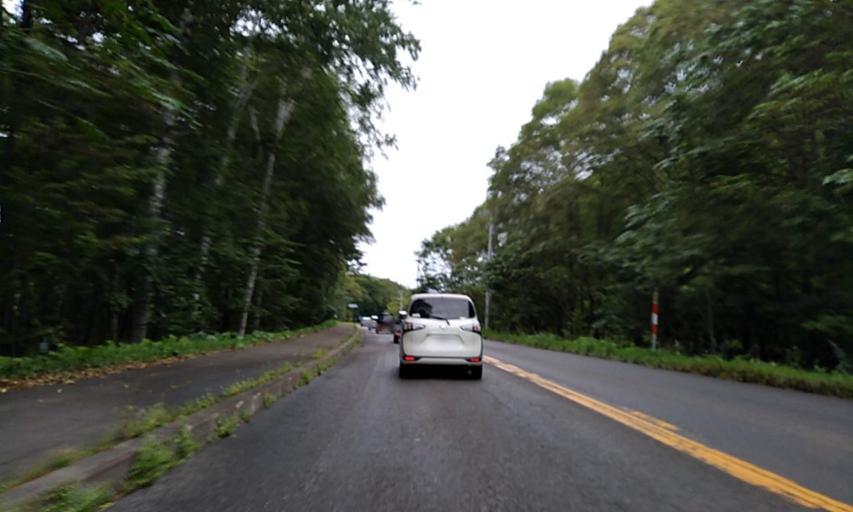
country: JP
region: Hokkaido
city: Abashiri
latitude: 43.9749
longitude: 144.2178
